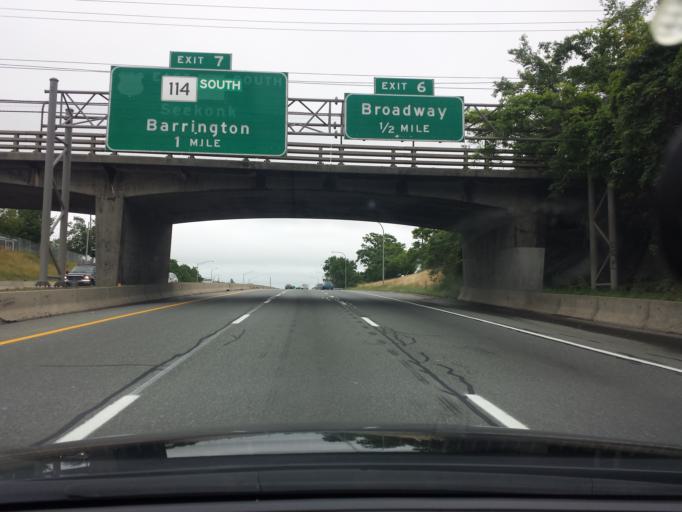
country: US
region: Rhode Island
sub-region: Providence County
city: East Providence
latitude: 41.8163
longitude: -71.3756
